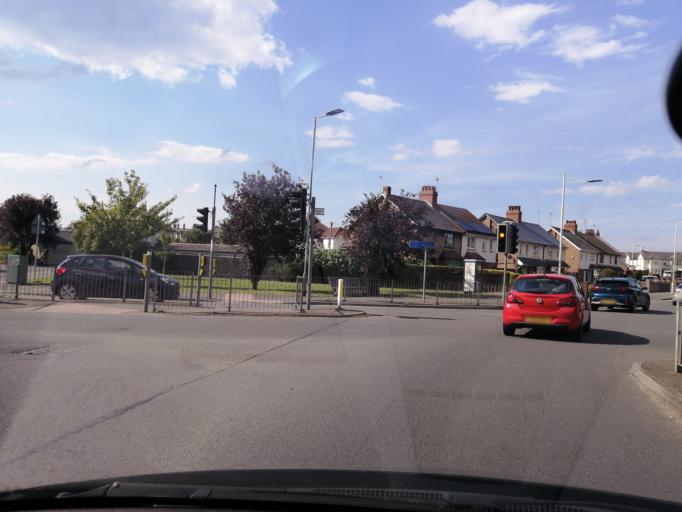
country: GB
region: England
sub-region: Peterborough
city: Peterborough
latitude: 52.5575
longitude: -0.2498
